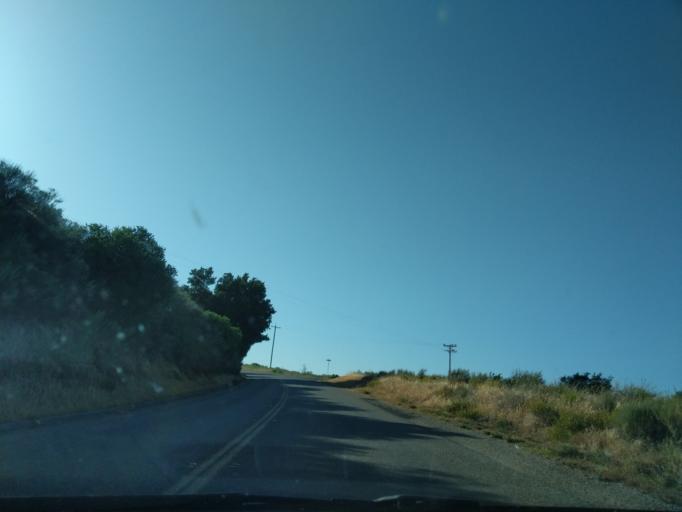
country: US
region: California
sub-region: Monterey County
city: Soledad
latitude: 36.4265
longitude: -121.4023
